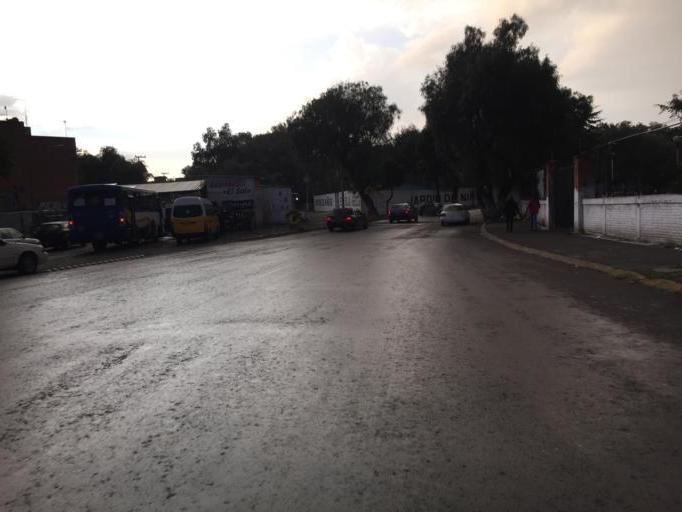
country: MX
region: Mexico
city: Cuautitlan Izcalli
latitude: 19.6741
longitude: -99.2145
